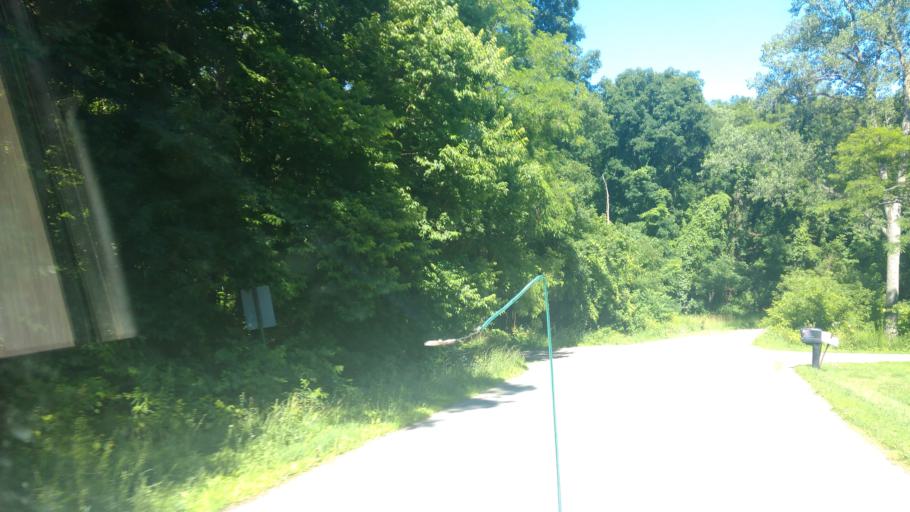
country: US
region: New York
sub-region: Wayne County
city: Clyde
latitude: 43.0267
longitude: -76.8753
